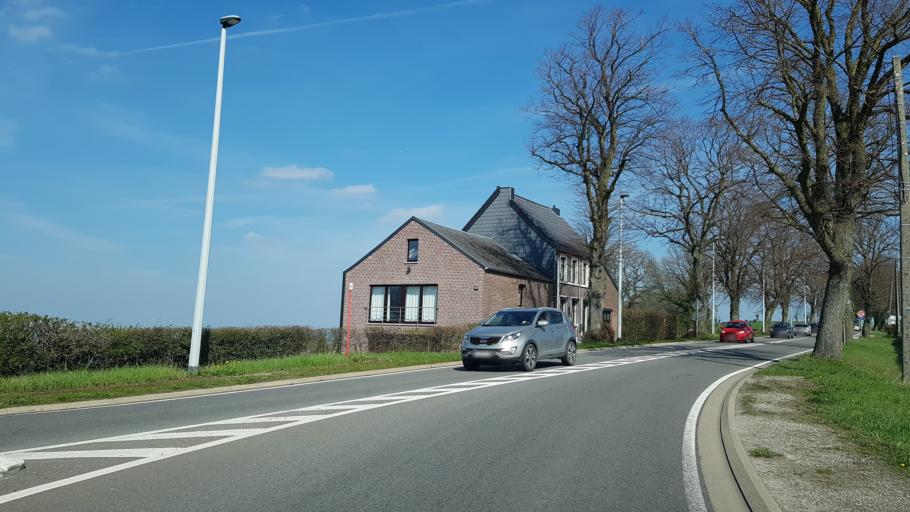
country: BE
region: Wallonia
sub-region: Province de Liege
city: Dison
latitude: 50.6512
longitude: 5.8834
